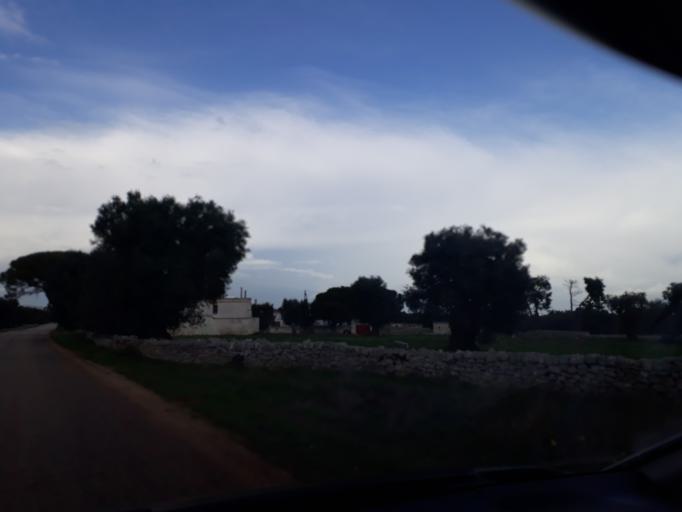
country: IT
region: Apulia
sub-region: Provincia di Brindisi
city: Pezze di Greco
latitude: 40.8062
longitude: 17.3911
